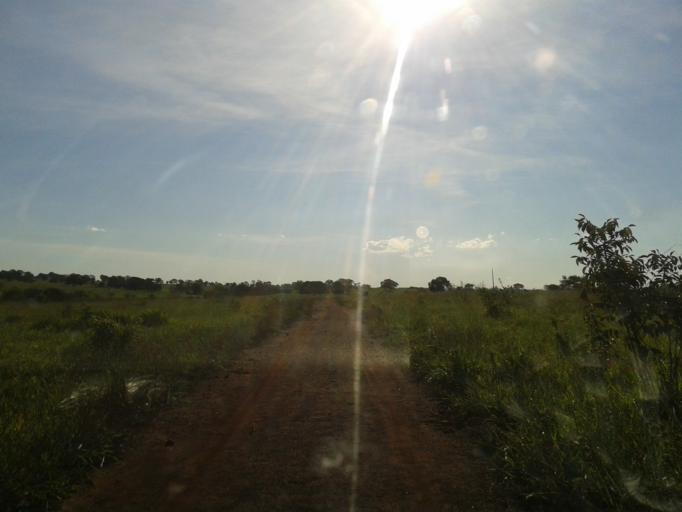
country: BR
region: Minas Gerais
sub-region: Santa Vitoria
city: Santa Vitoria
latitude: -18.9993
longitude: -50.3479
